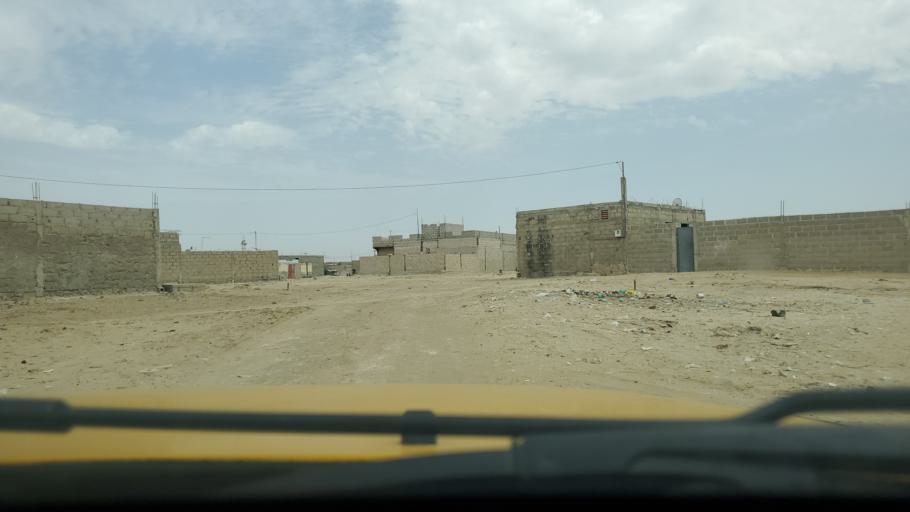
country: SN
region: Saint-Louis
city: Saint-Louis
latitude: 16.0329
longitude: -16.4617
